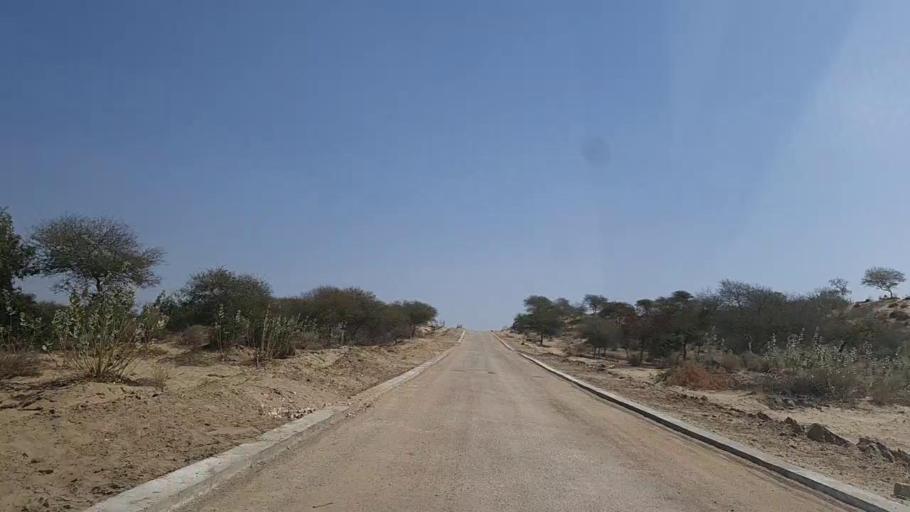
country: PK
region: Sindh
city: Diplo
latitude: 24.4781
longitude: 69.5048
